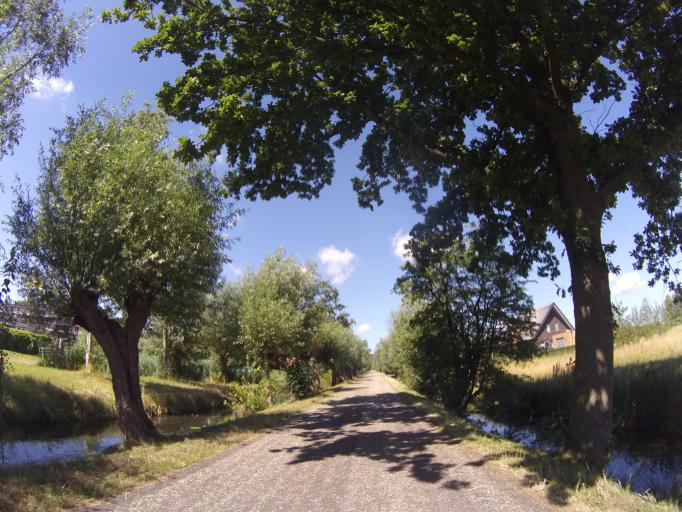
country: NL
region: Utrecht
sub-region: Stichtse Vecht
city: Spechtenkamp
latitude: 52.1111
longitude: 5.0254
